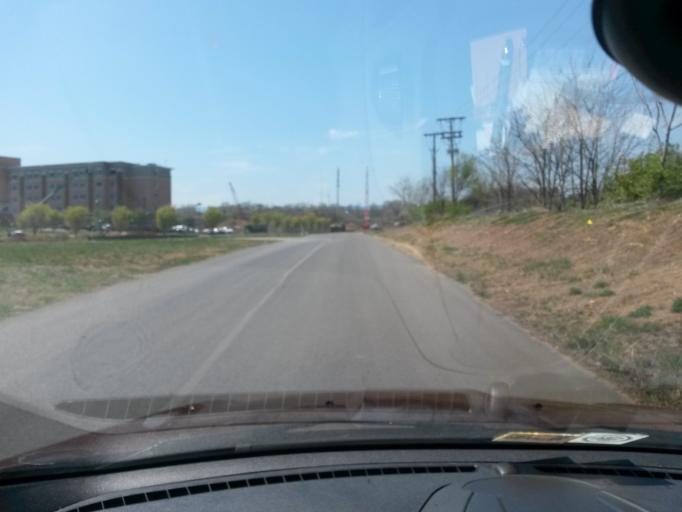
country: US
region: Virginia
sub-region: City of Roanoke
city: Cedar Bluff
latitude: 37.2572
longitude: -79.9452
